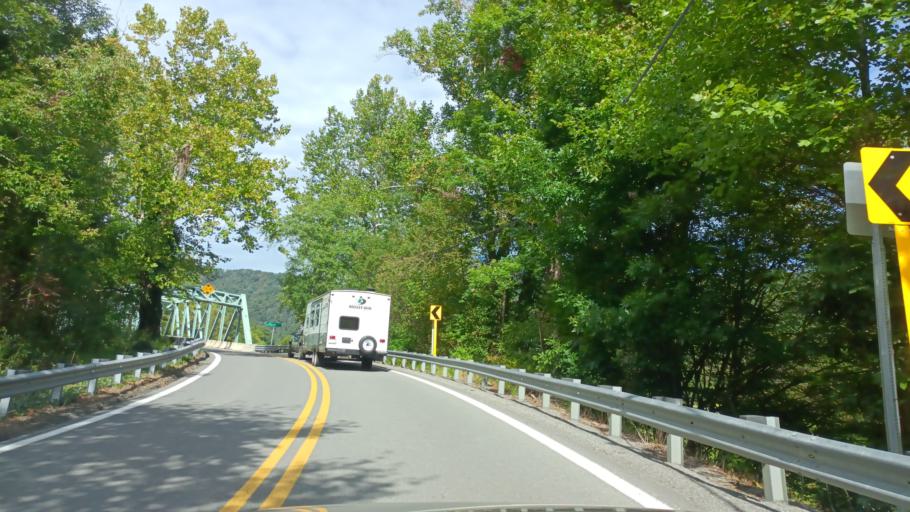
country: US
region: West Virginia
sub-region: Preston County
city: Kingwood
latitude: 39.3192
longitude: -79.6553
